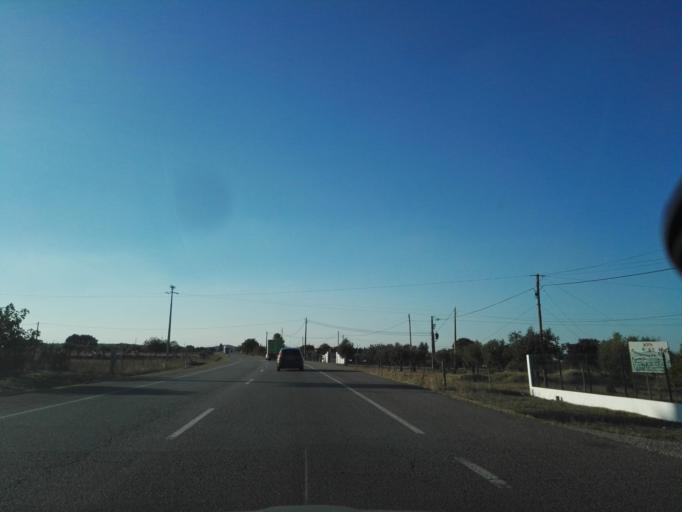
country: PT
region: Evora
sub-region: Borba
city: Borba
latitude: 38.8177
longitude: -7.4838
